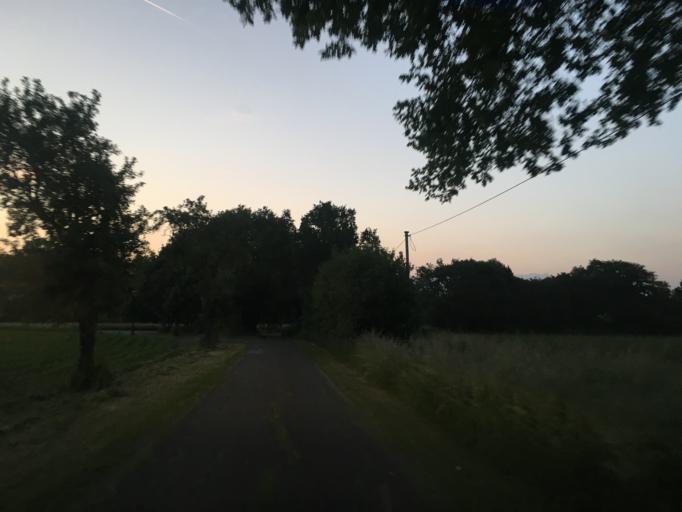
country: DE
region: North Rhine-Westphalia
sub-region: Regierungsbezirk Munster
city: Muenster
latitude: 52.0118
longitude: 7.5852
